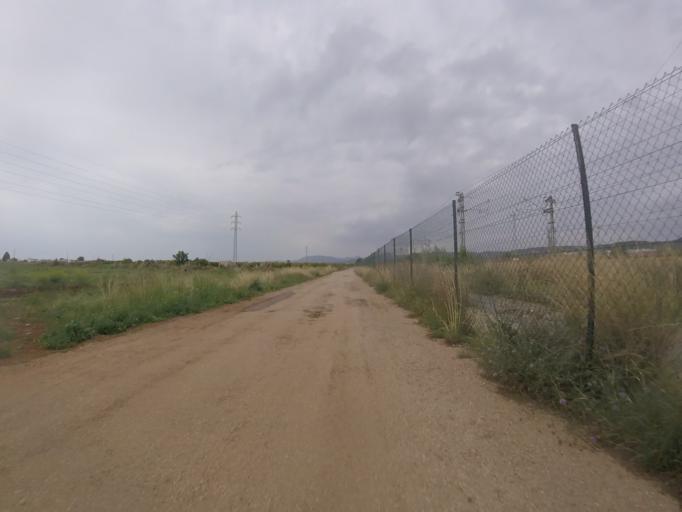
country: ES
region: Valencia
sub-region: Provincia de Castello
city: Torreblanca
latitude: 40.2180
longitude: 0.2055
